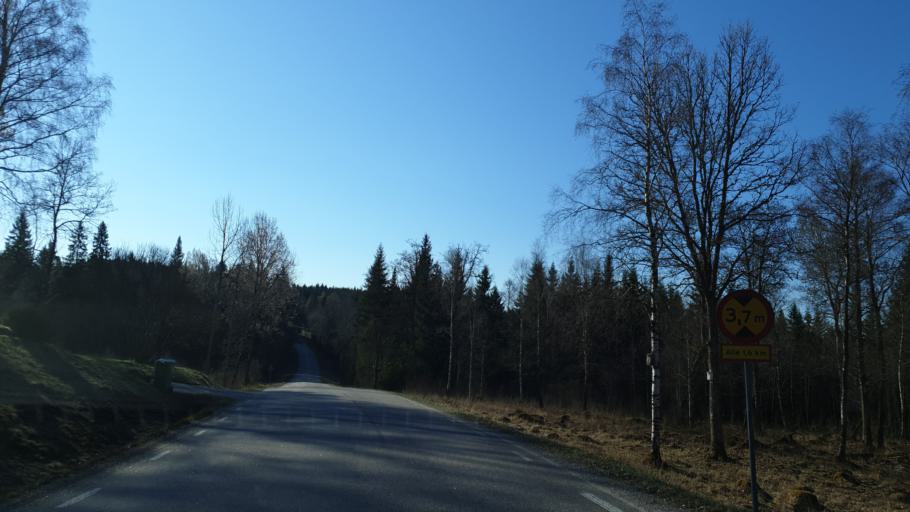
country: SE
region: Vaestra Goetaland
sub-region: Boras Kommun
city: Dalsjofors
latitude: 57.7854
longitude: 13.0896
